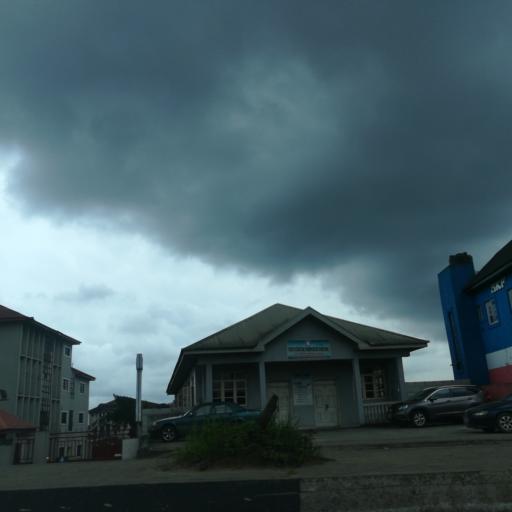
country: NG
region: Rivers
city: Port Harcourt
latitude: 4.8284
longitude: 7.0367
